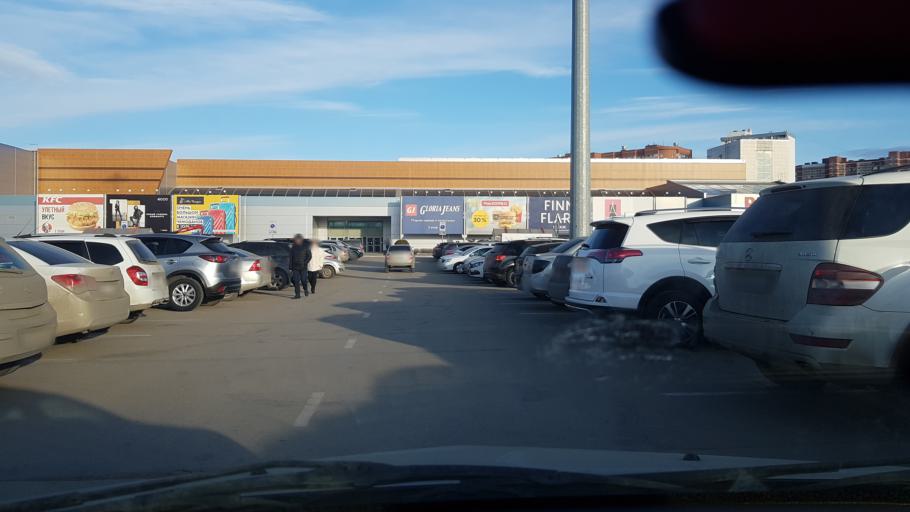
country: RU
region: Samara
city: Tol'yatti
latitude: 53.5402
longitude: 49.3896
